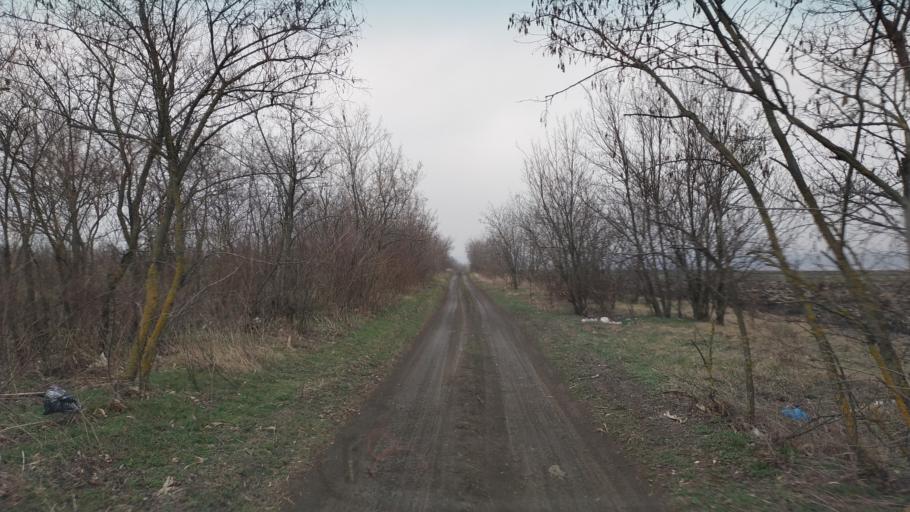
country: MD
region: Chisinau
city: Singera
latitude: 46.8262
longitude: 28.9880
